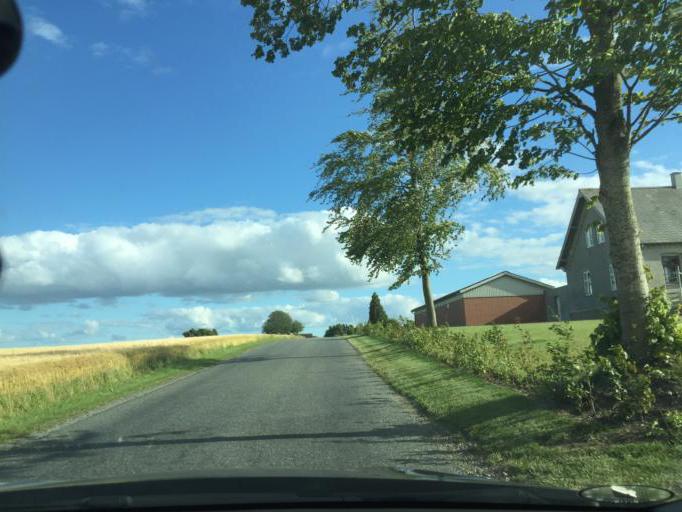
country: DK
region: South Denmark
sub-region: Faaborg-Midtfyn Kommune
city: Arslev
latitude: 55.2930
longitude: 10.5395
